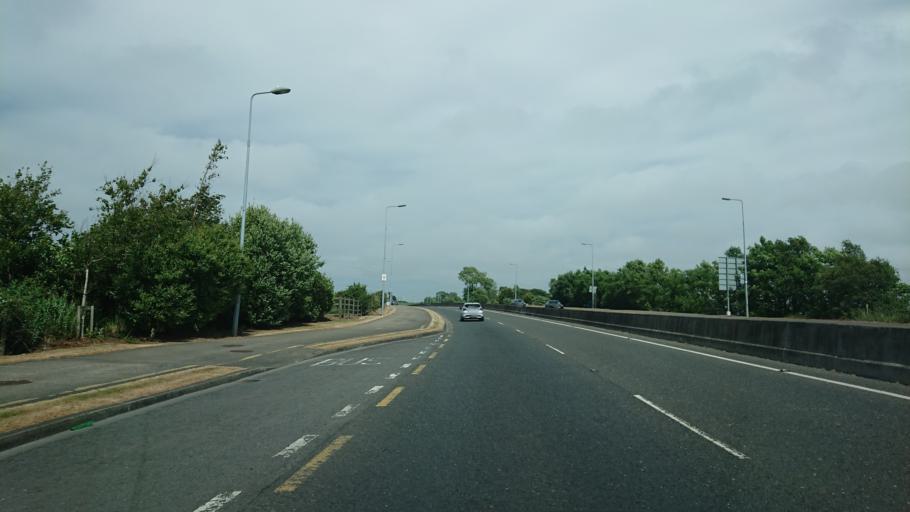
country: IE
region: Munster
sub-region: Waterford
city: Waterford
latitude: 52.2343
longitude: -7.1027
